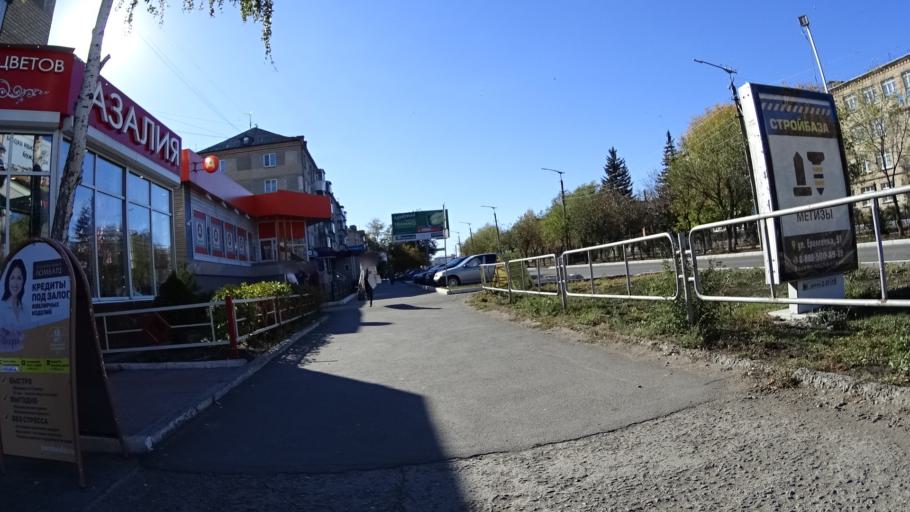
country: RU
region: Chelyabinsk
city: Troitsk
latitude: 54.0819
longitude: 61.5372
